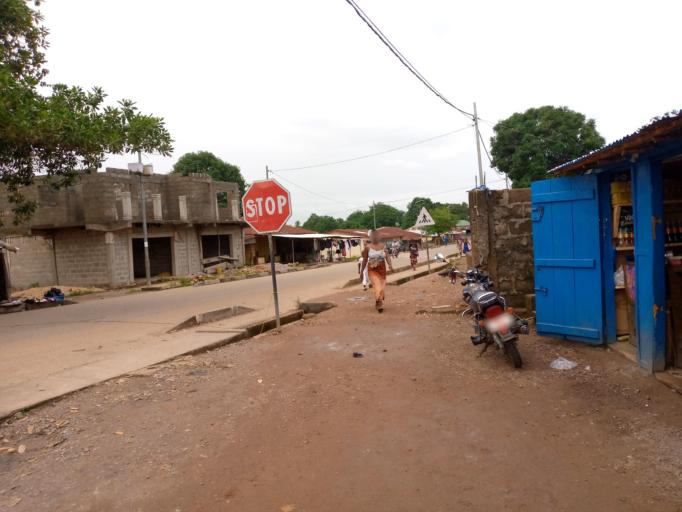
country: SL
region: Northern Province
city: Magburaka
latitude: 8.7216
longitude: -11.9518
